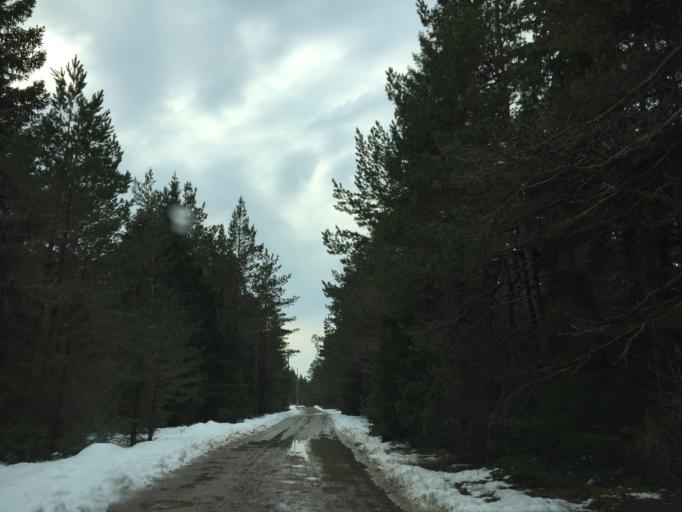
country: EE
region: Saare
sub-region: Kuressaare linn
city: Kuressaare
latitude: 58.4399
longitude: 22.1338
